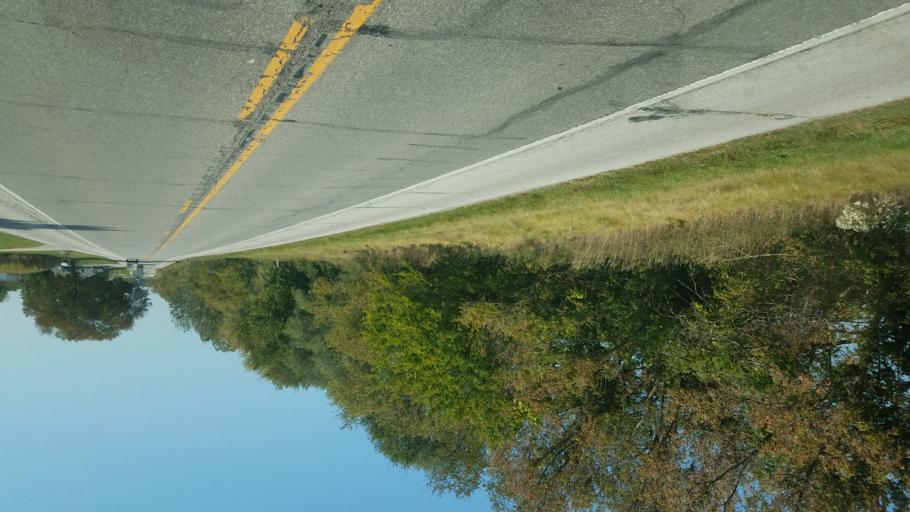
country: US
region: Indiana
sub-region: LaGrange County
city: Lagrange
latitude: 41.6421
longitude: -85.3370
